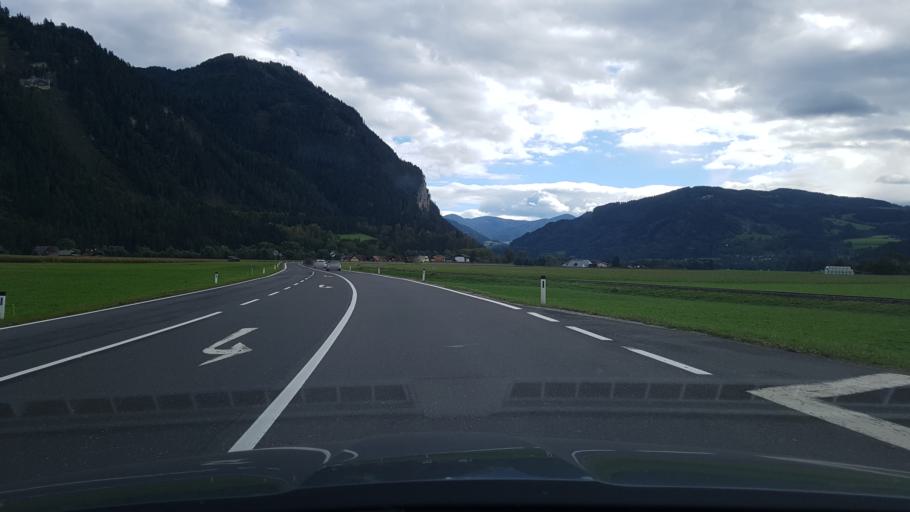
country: AT
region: Styria
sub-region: Politischer Bezirk Murau
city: Teufenbach
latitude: 47.1322
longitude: 14.3210
